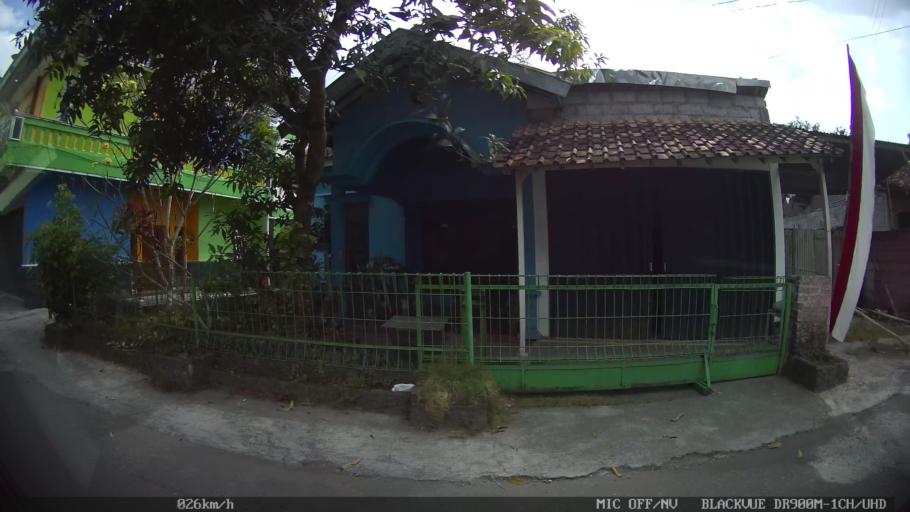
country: ID
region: Daerah Istimewa Yogyakarta
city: Gamping Lor
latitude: -7.8056
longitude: 110.3279
